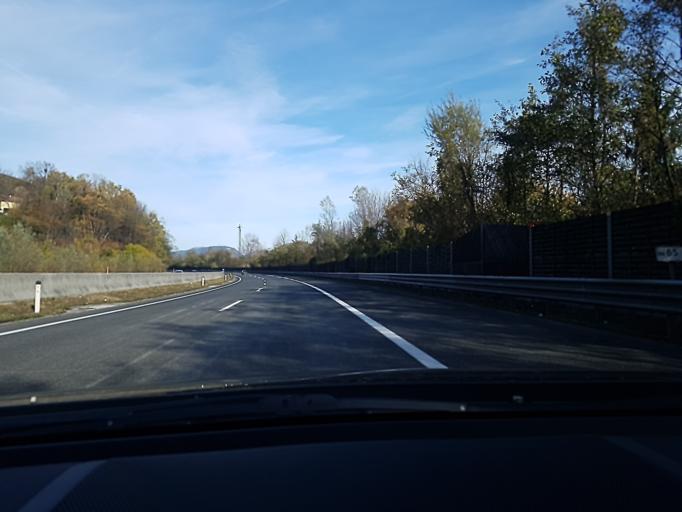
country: AT
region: Salzburg
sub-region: Politischer Bezirk Hallein
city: Kuchl
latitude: 47.6184
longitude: 13.1389
